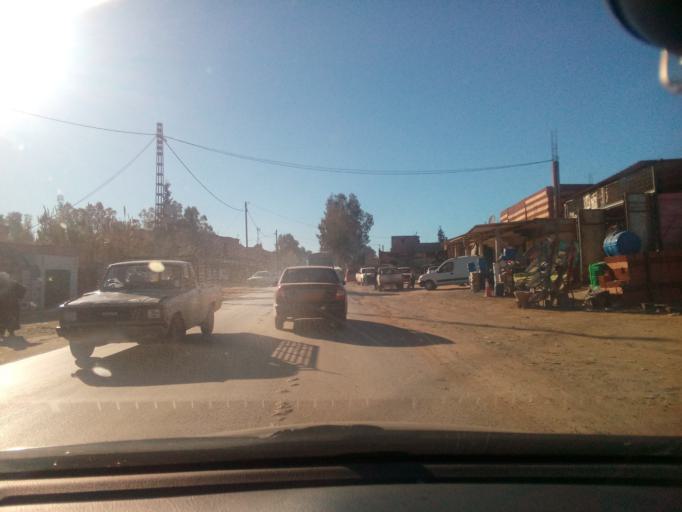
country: DZ
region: Mostaganem
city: Mostaganem
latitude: 35.8973
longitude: 0.2606
